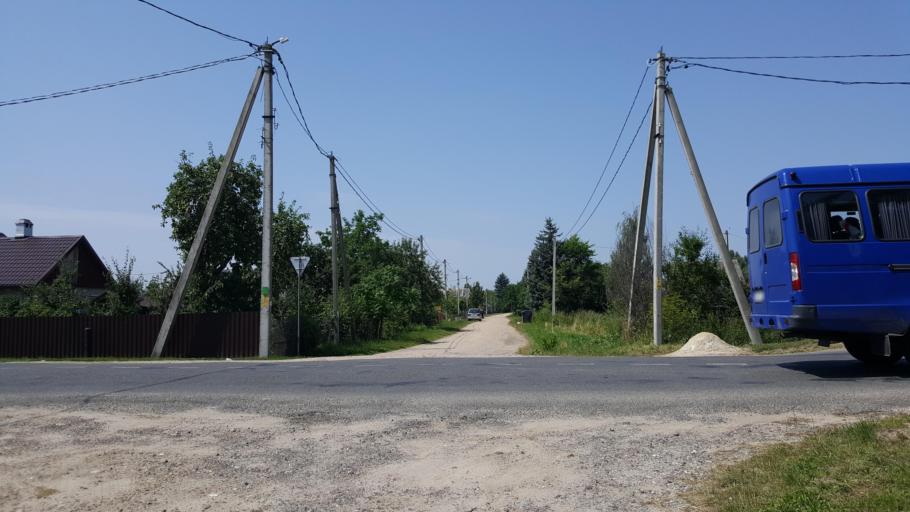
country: BY
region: Brest
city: Zhabinka
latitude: 52.1897
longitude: 24.0027
